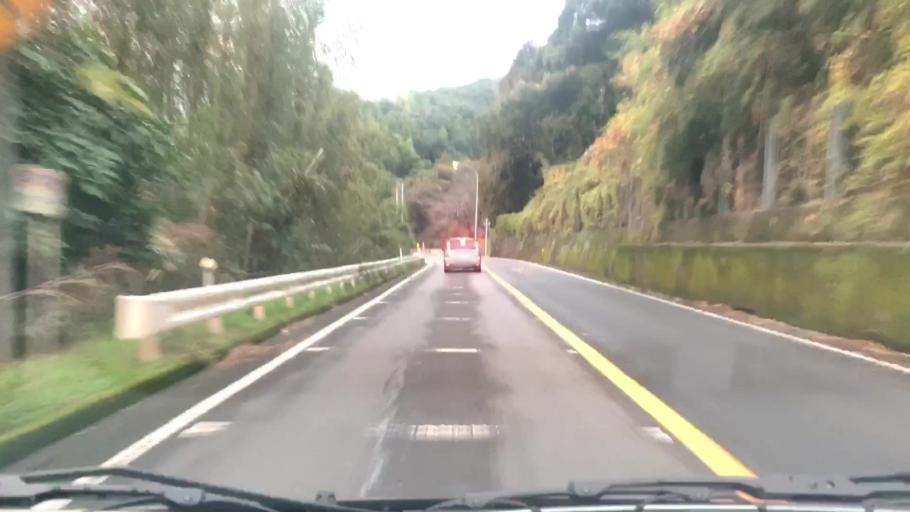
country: JP
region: Saga Prefecture
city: Ureshinomachi-shimojuku
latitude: 33.0610
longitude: 129.9559
